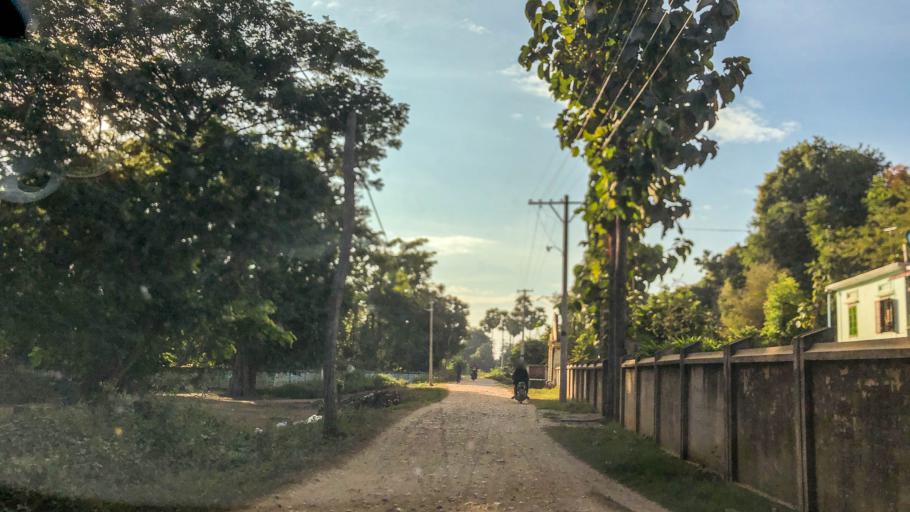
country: MM
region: Magway
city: Magway
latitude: 19.9764
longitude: 95.0346
